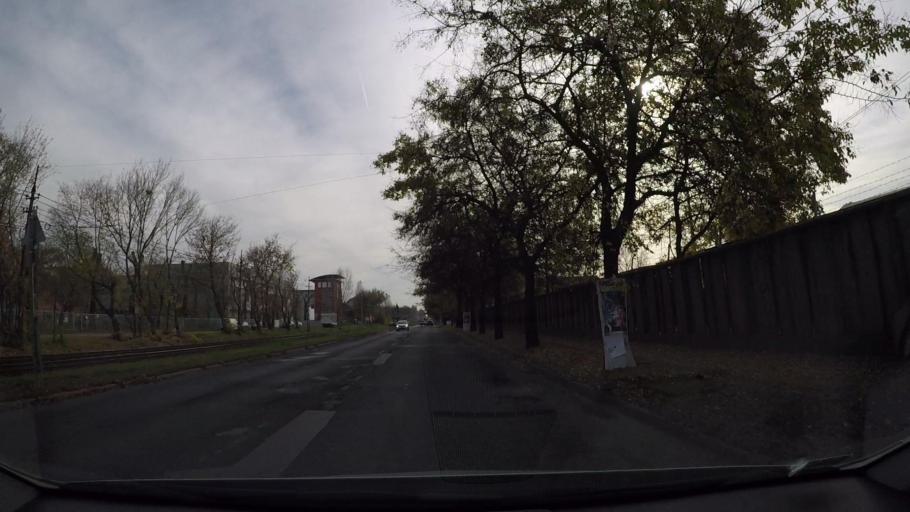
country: HU
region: Budapest
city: Budapest X. keruelet
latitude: 47.4888
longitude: 19.1505
